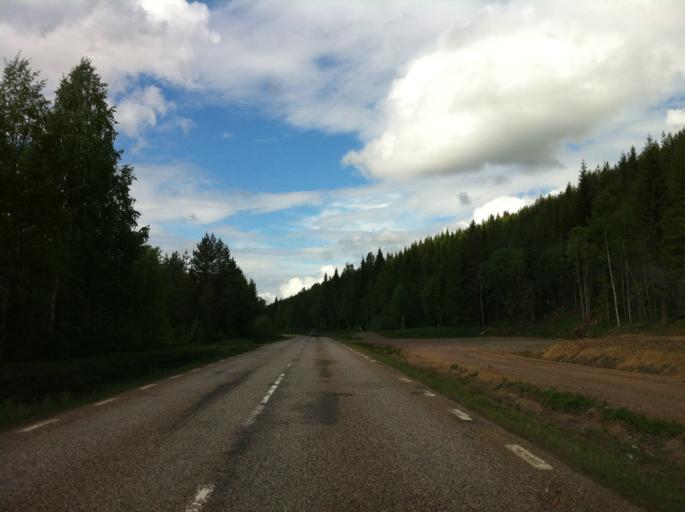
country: SE
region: Dalarna
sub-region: Malung-Saelens kommun
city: Malung
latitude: 61.1959
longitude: 13.2308
